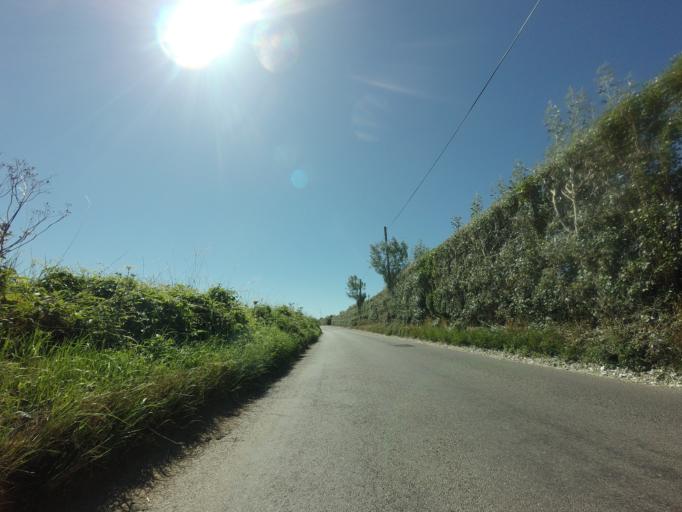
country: GB
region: England
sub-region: Kent
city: Ash
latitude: 51.2813
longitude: 1.2600
